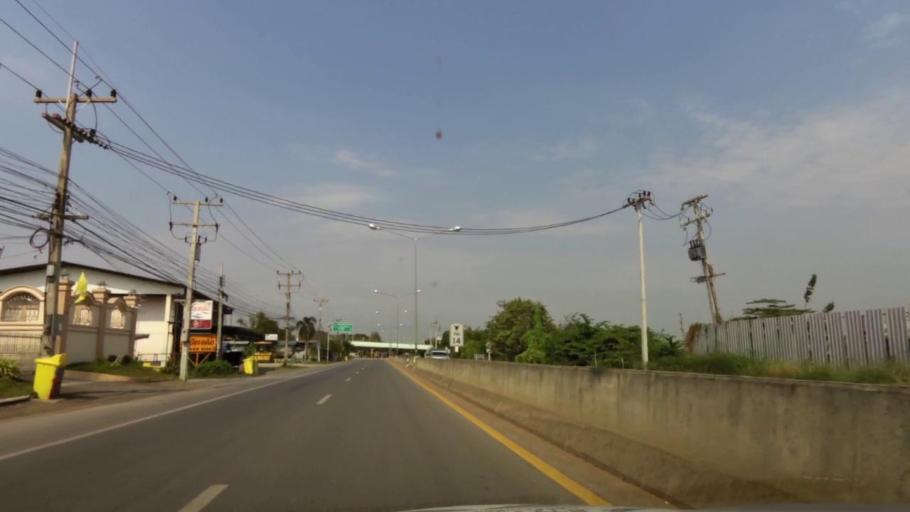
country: TH
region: Phra Nakhon Si Ayutthaya
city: Phra Nakhon Si Ayutthaya
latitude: 14.3291
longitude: 100.5769
